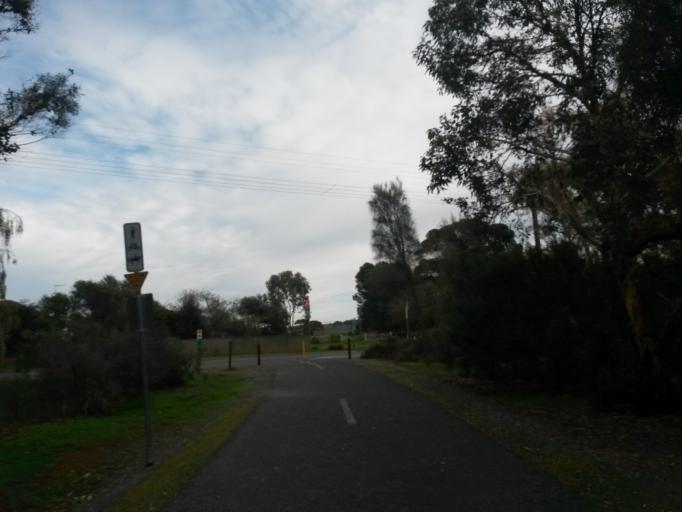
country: AU
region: South Australia
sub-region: Onkaparinga
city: McLaren Vale
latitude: -35.2128
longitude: 138.5308
